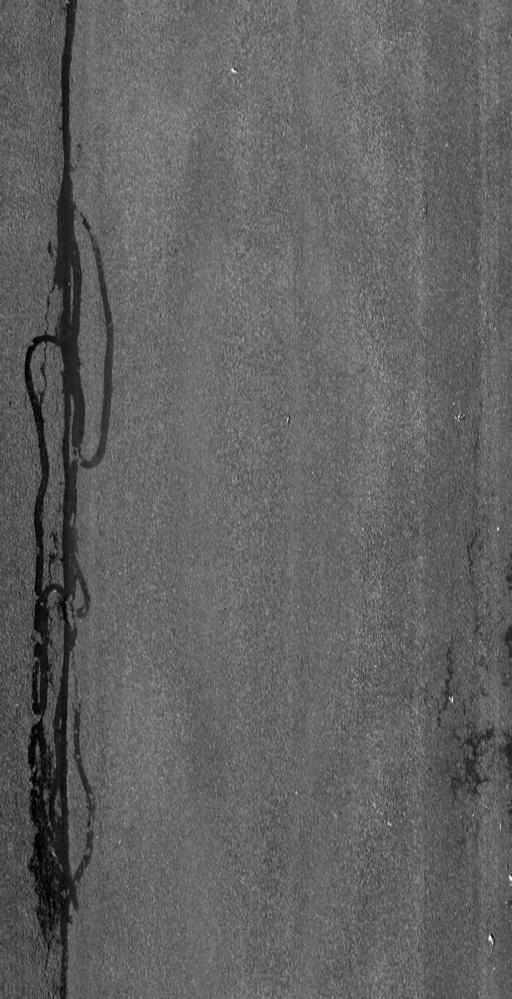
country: US
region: Vermont
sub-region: Chittenden County
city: Burlington
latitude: 44.5258
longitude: -73.2674
